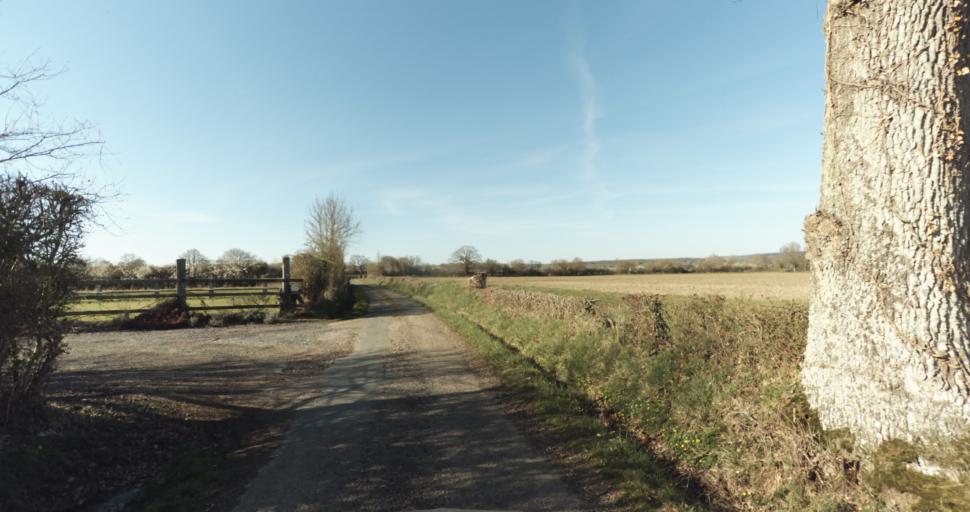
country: FR
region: Lower Normandy
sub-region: Departement du Calvados
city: Saint-Pierre-sur-Dives
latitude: 49.0413
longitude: 0.0531
